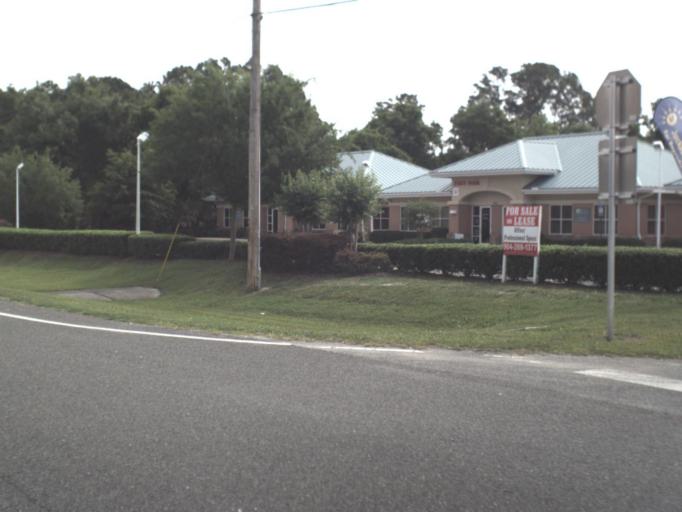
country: US
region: Florida
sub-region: Clay County
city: Orange Park
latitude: 30.1367
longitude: -81.7020
